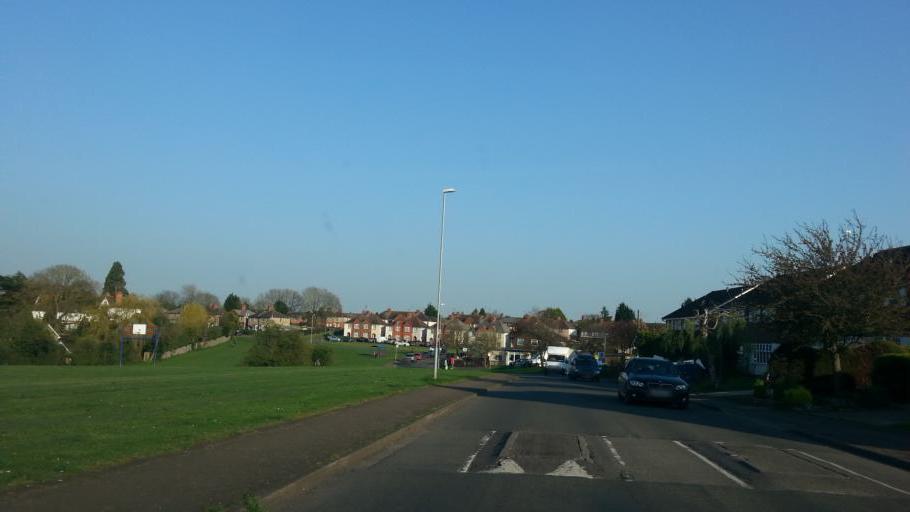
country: GB
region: England
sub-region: Northamptonshire
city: Rushden
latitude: 52.2914
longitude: -0.6193
